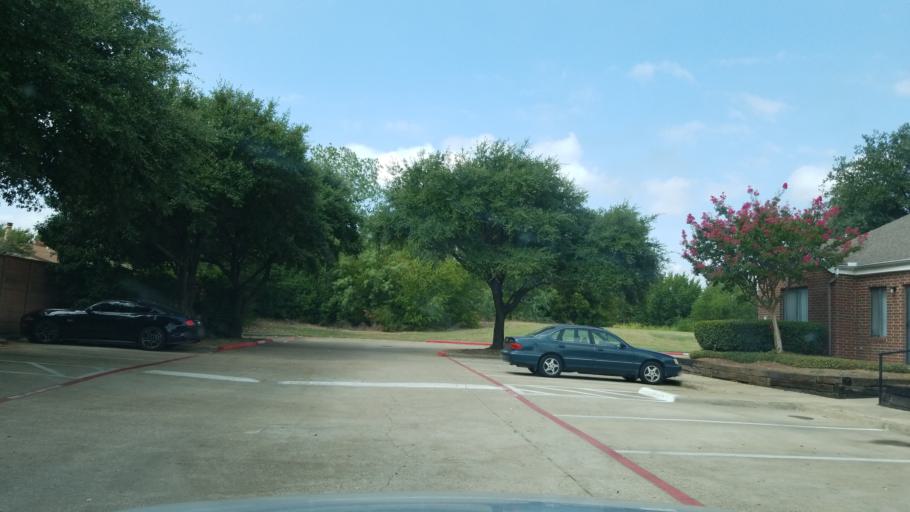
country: US
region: Texas
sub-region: Tarrant County
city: Euless
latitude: 32.8503
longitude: -97.1045
